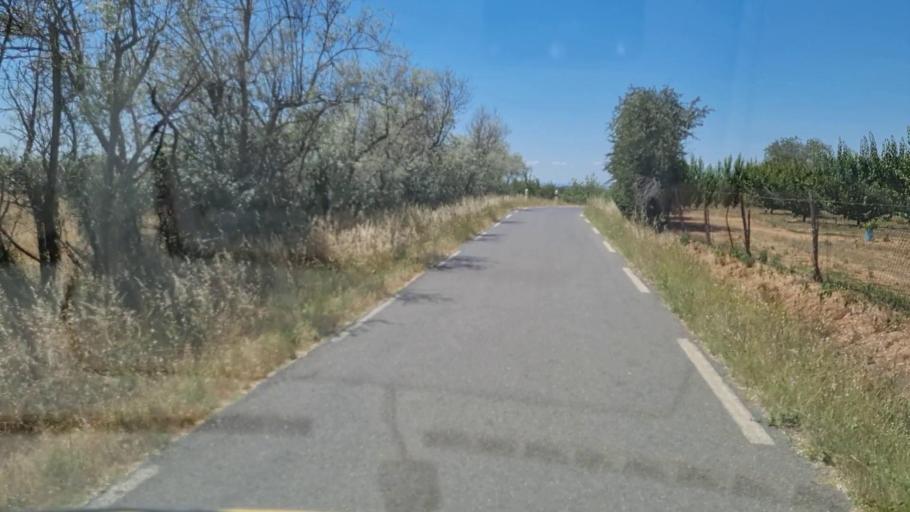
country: FR
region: Languedoc-Roussillon
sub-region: Departement du Gard
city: Le Cailar
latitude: 43.6268
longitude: 4.2509
